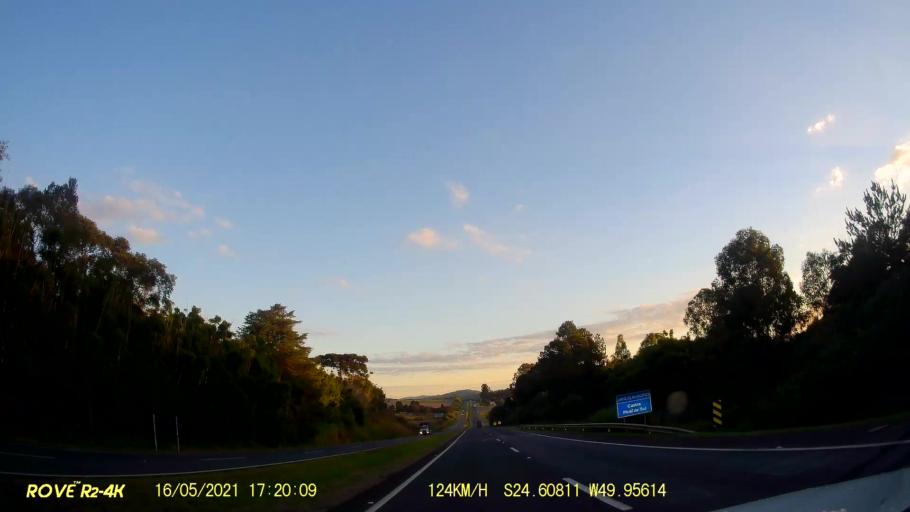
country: BR
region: Parana
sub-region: Pirai Do Sul
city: Pirai do Sul
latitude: -24.6086
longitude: -49.9562
